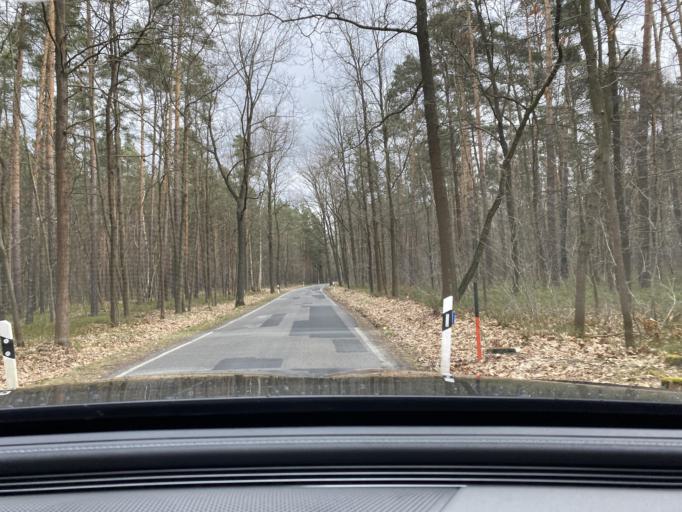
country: DE
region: Saxony
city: Uhyst
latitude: 51.3251
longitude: 14.4719
